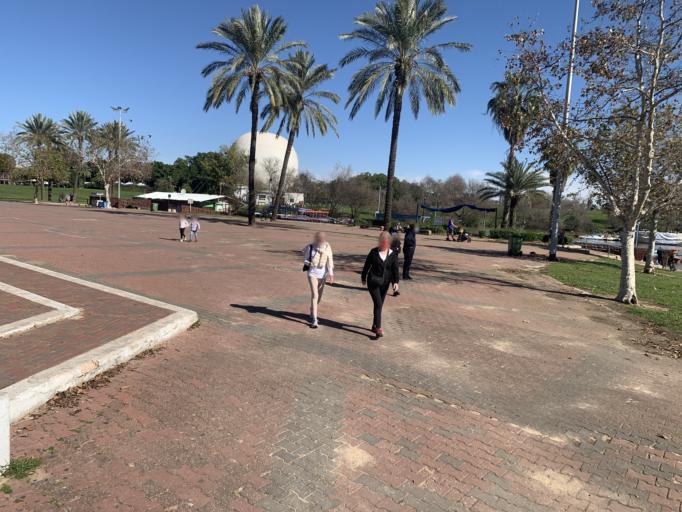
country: IL
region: Tel Aviv
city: Ramat Gan
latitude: 32.0984
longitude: 34.8092
